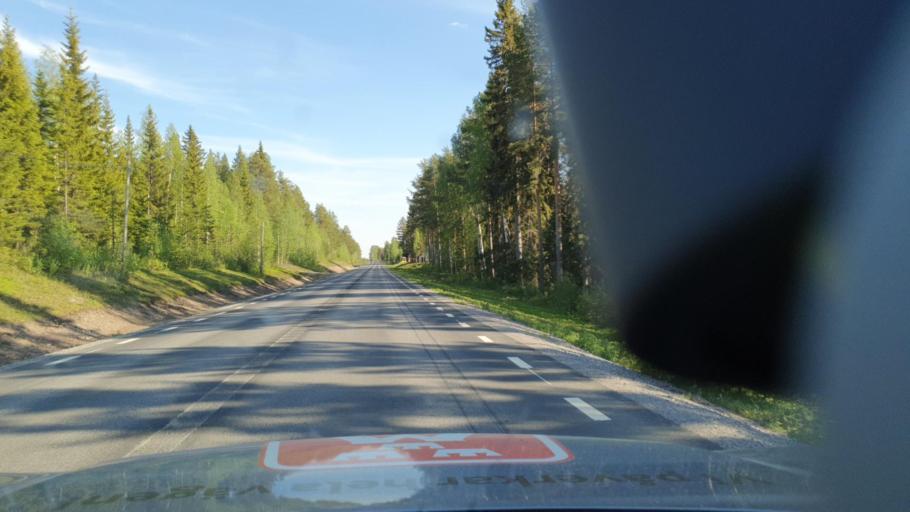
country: SE
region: Norrbotten
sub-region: Alvsbyns Kommun
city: AElvsbyn
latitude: 66.1172
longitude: 20.9252
